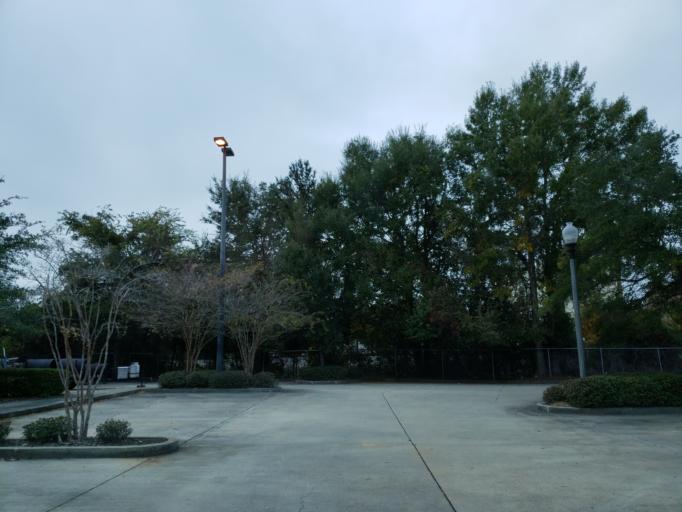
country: US
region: Mississippi
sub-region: Forrest County
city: Hattiesburg
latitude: 31.3247
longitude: -89.2894
